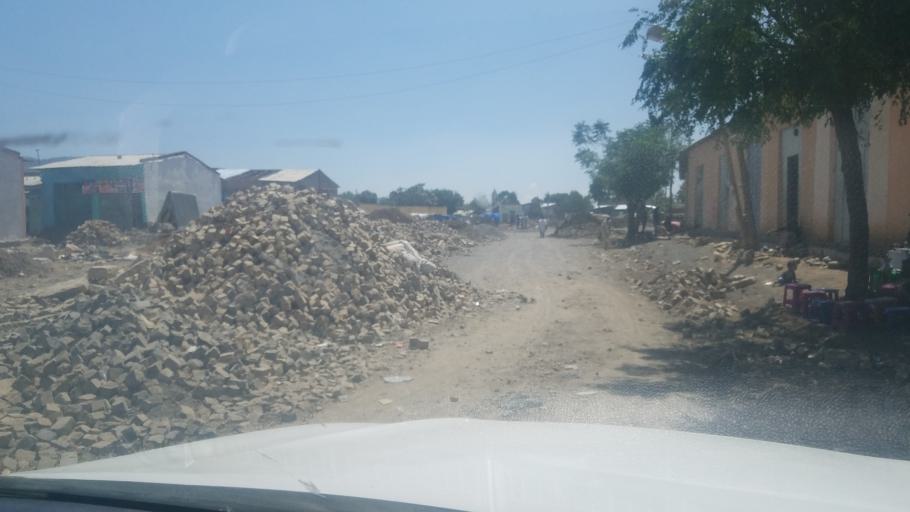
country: ET
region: Tigray
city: Mekele
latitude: 13.7951
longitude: 39.5988
